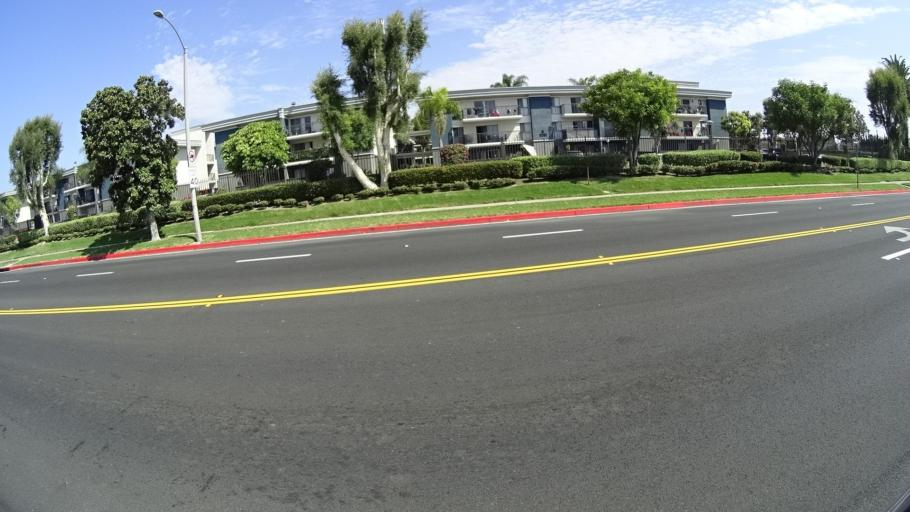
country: US
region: California
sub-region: Orange County
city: Stanton
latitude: 33.8294
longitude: -117.9599
